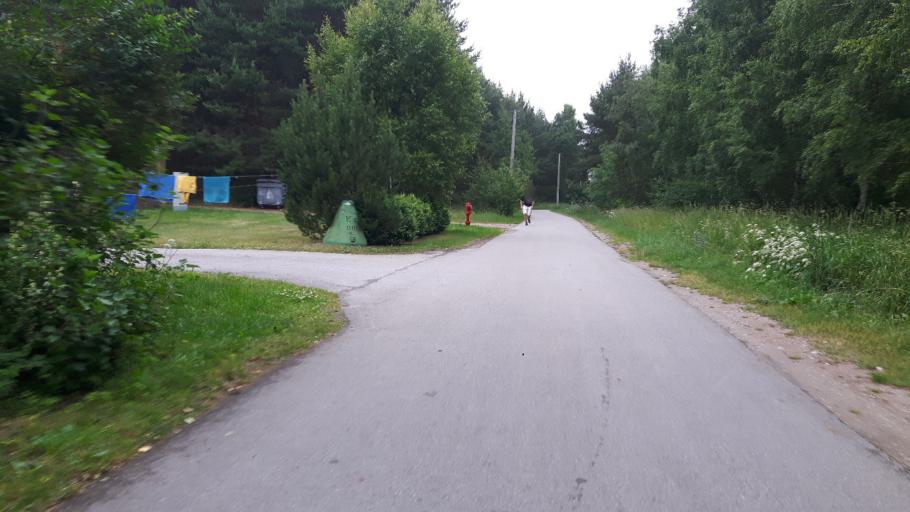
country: LT
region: Klaipedos apskritis
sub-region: Palanga
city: Sventoji
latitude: 55.9949
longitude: 21.0757
